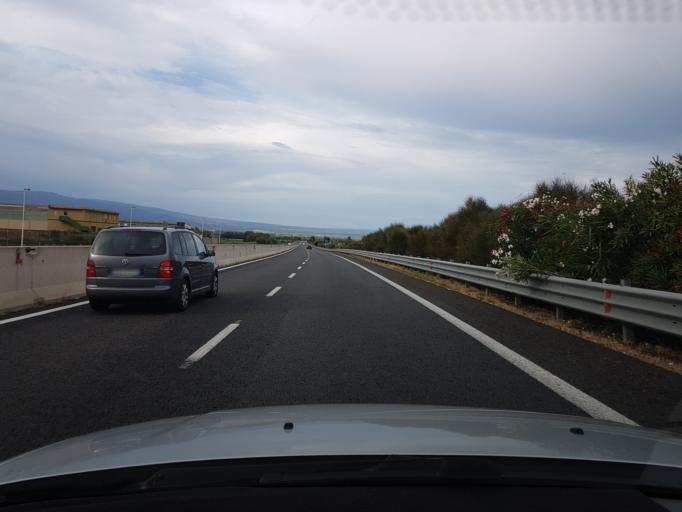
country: IT
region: Sardinia
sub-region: Provincia di Oristano
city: Siamaggiore
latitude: 39.9718
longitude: 8.6266
